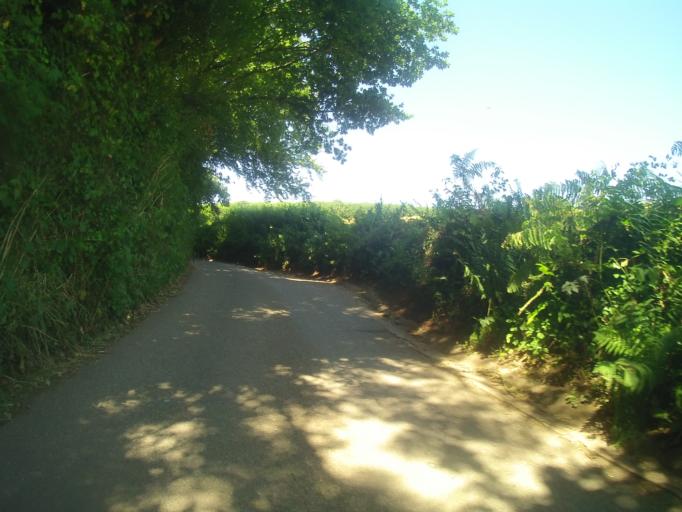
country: GB
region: England
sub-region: Devon
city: Totnes
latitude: 50.3680
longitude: -3.6506
